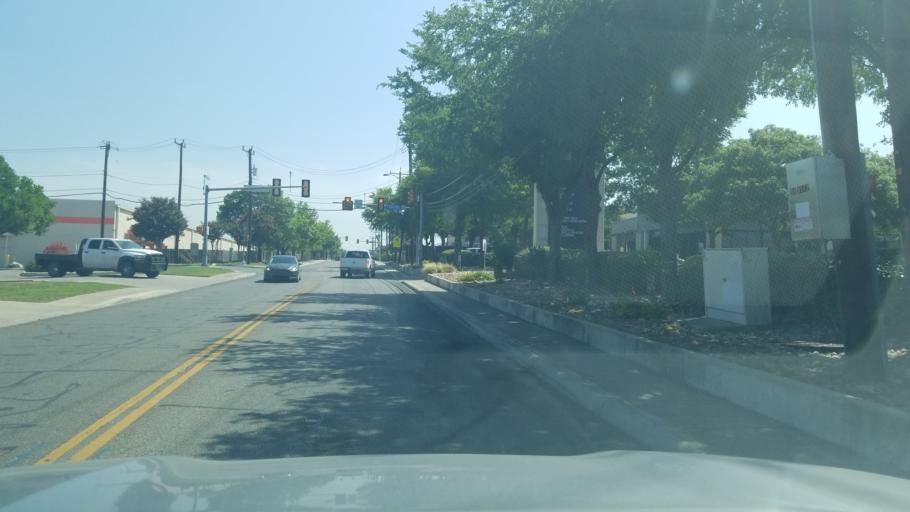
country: US
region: Texas
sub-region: Bexar County
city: Hollywood Park
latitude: 29.5646
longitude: -98.4788
